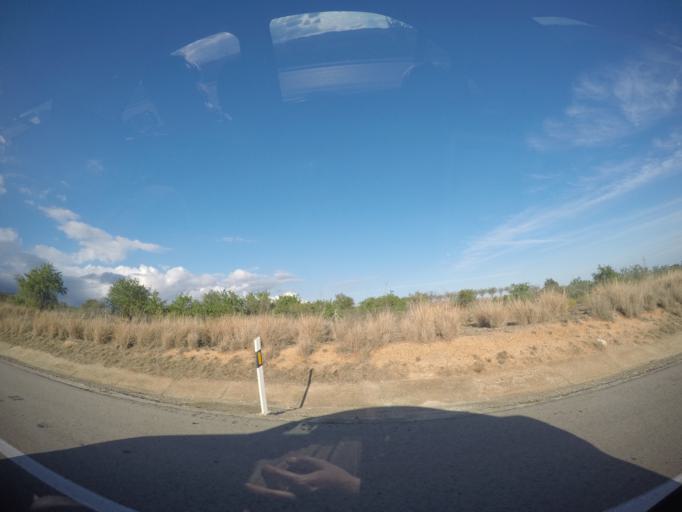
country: ES
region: Catalonia
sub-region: Provincia de Tarragona
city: la Bisbal del Penedes
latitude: 41.2814
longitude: 1.4975
